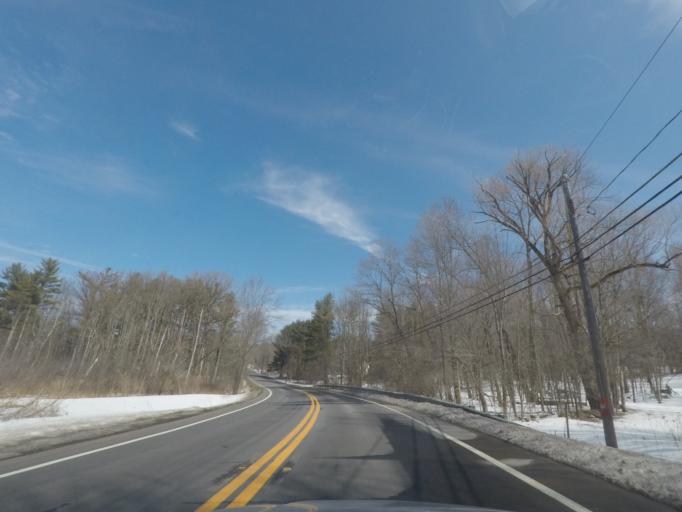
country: US
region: Massachusetts
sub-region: Berkshire County
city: Richmond
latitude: 42.3663
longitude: -73.3716
